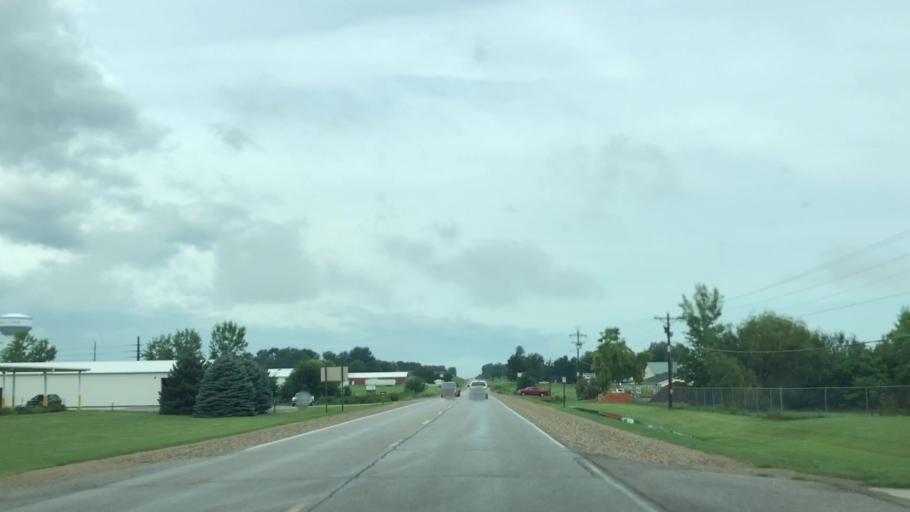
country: US
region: Iowa
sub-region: Marshall County
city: Marshalltown
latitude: 42.0074
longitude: -92.9345
